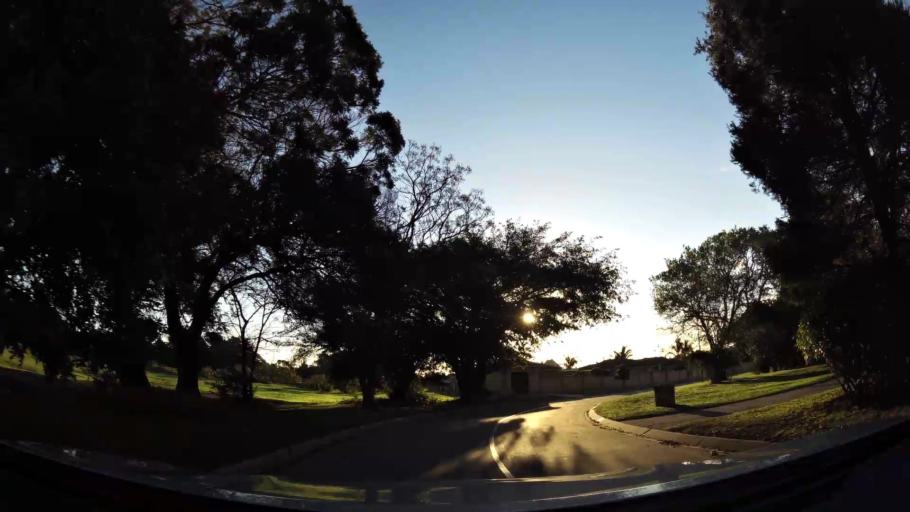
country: ZA
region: Eastern Cape
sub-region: Nelson Mandela Bay Metropolitan Municipality
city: Port Elizabeth
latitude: -33.9685
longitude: 25.4900
